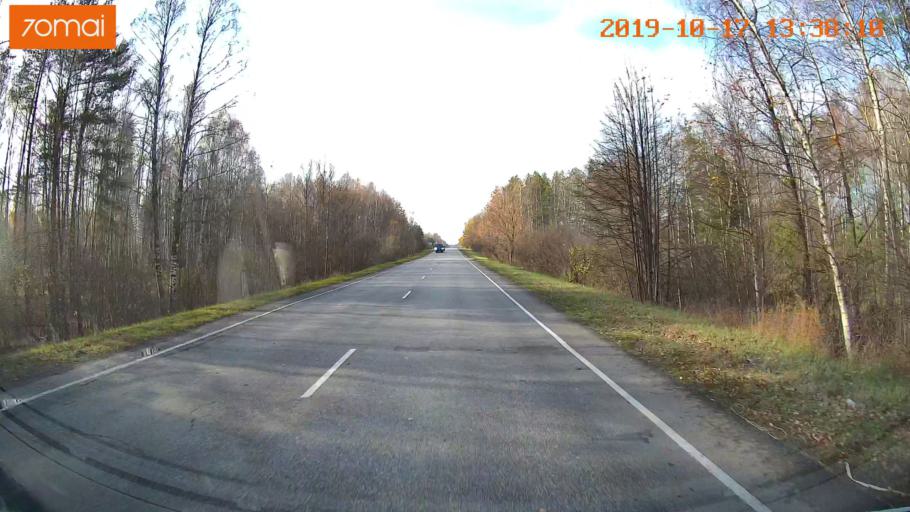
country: RU
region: Rjazan
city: Tuma
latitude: 55.1433
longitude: 40.6205
